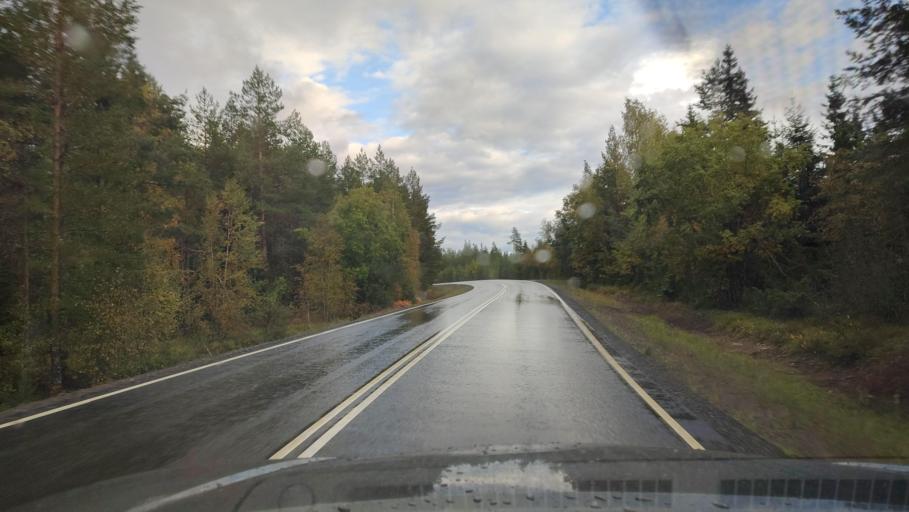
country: FI
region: Southern Ostrobothnia
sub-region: Suupohja
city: Karijoki
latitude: 62.2906
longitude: 21.6498
